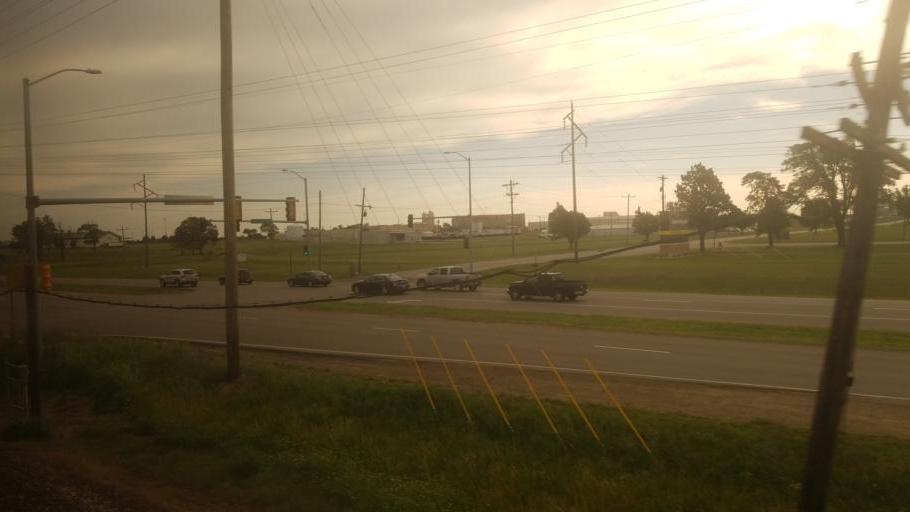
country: US
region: Kansas
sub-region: Shawnee County
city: Topeka
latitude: 38.9524
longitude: -95.6876
